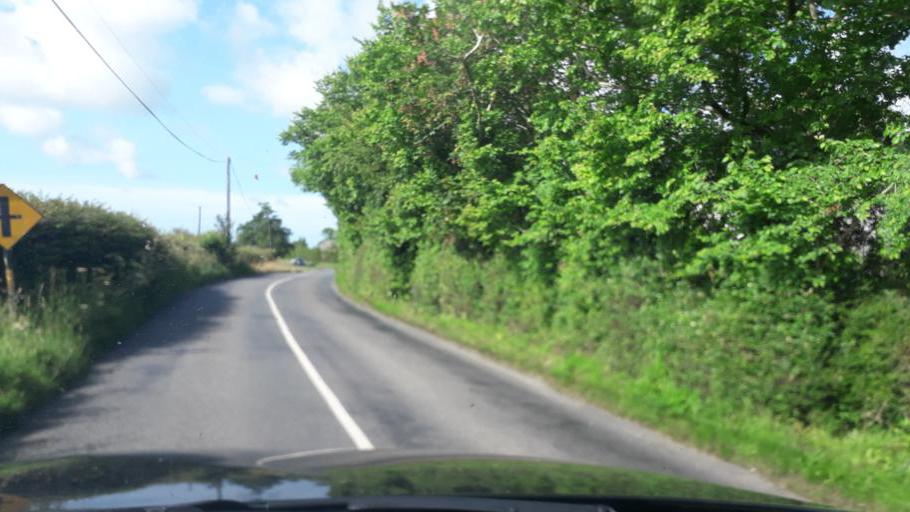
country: IE
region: Leinster
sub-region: Loch Garman
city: Loch Garman
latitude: 52.2654
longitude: -6.5574
